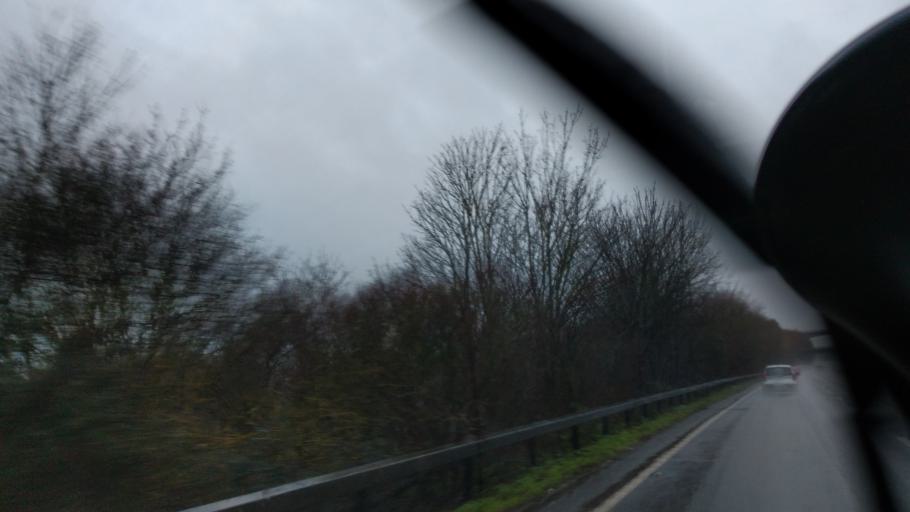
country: GB
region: England
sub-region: East Sussex
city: Lewes
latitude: 50.8664
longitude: 0.0028
